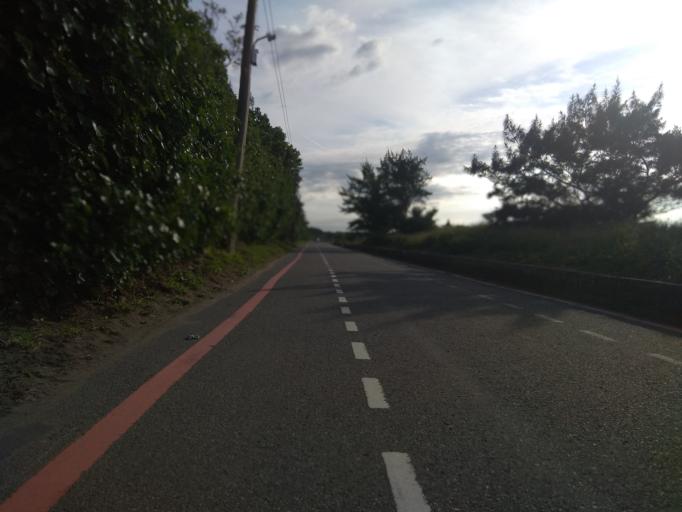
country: TW
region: Taiwan
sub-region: Hsinchu
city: Zhubei
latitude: 24.9799
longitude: 121.0162
